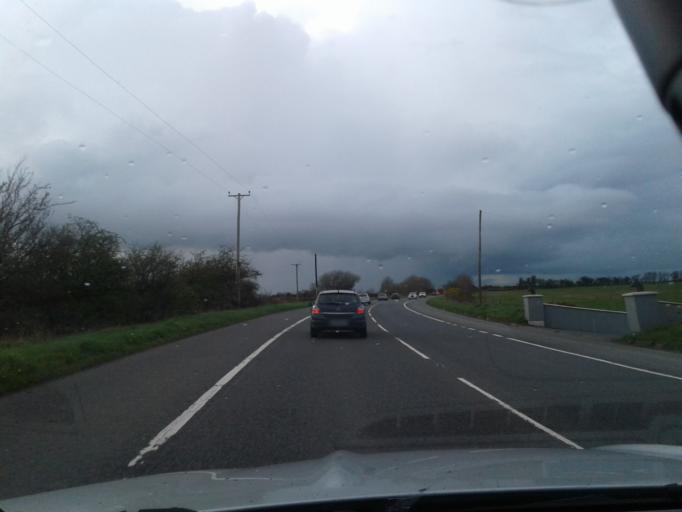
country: GB
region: Northern Ireland
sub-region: Strabane District
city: Sion Mills
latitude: 54.7390
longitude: -7.4362
